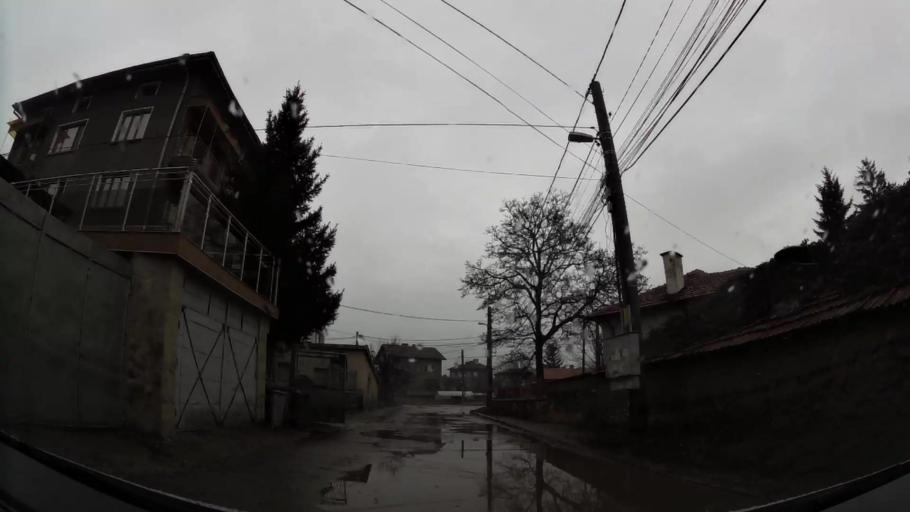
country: BG
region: Sofia-Capital
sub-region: Stolichna Obshtina
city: Sofia
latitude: 42.6303
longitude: 23.4050
